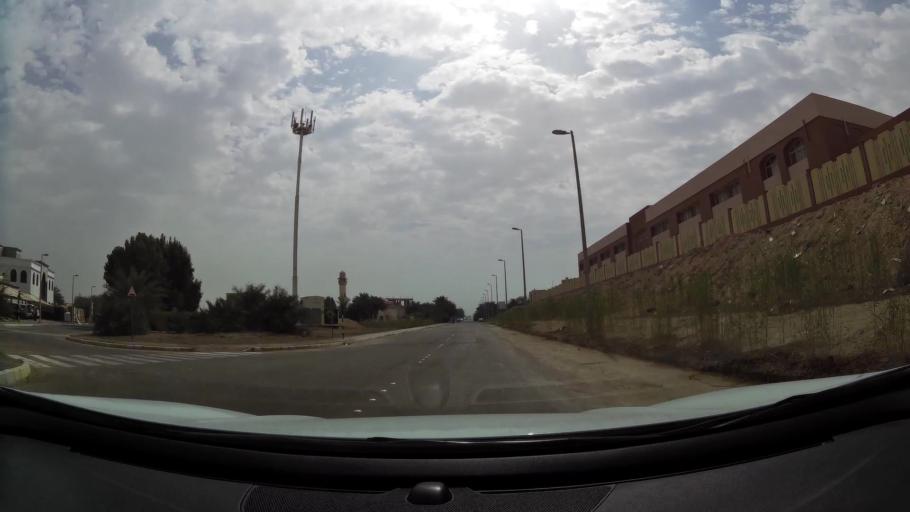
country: AE
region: Abu Dhabi
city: Abu Dhabi
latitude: 24.3268
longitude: 54.6304
